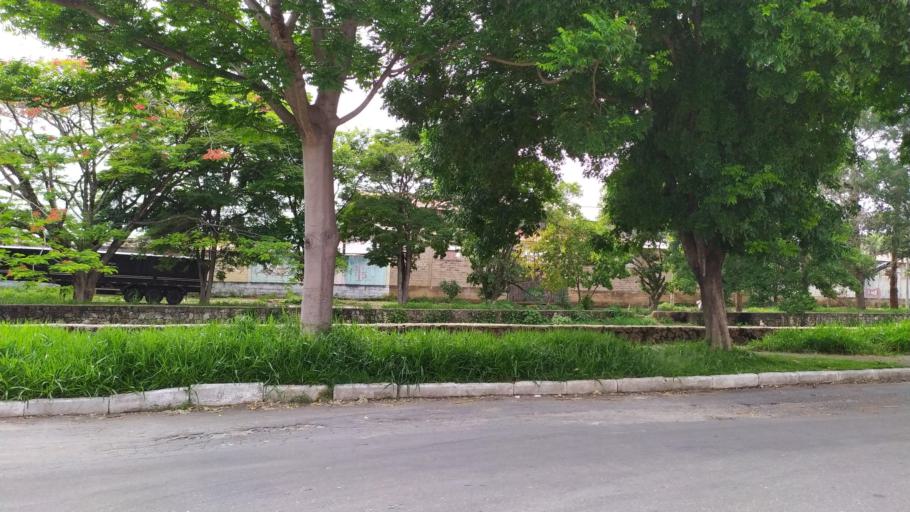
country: BR
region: Minas Gerais
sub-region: Sao Joao Del Rei
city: Sao Joao del Rei
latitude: -21.1247
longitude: -44.2457
